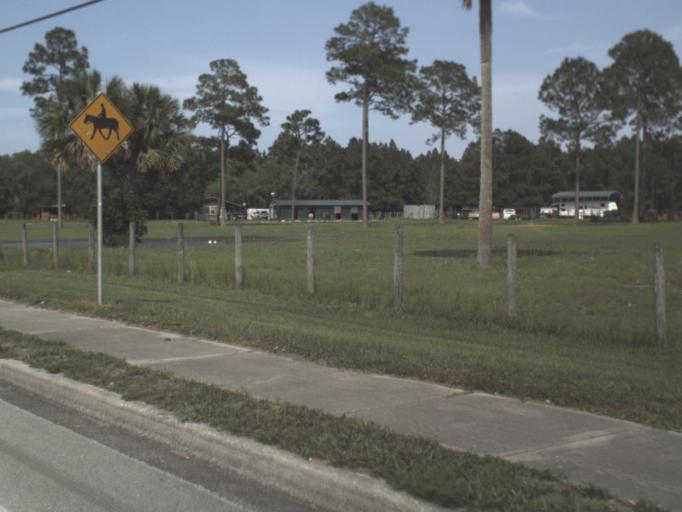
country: US
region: Florida
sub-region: Saint Johns County
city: Saint Augustine South
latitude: 29.8402
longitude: -81.3668
